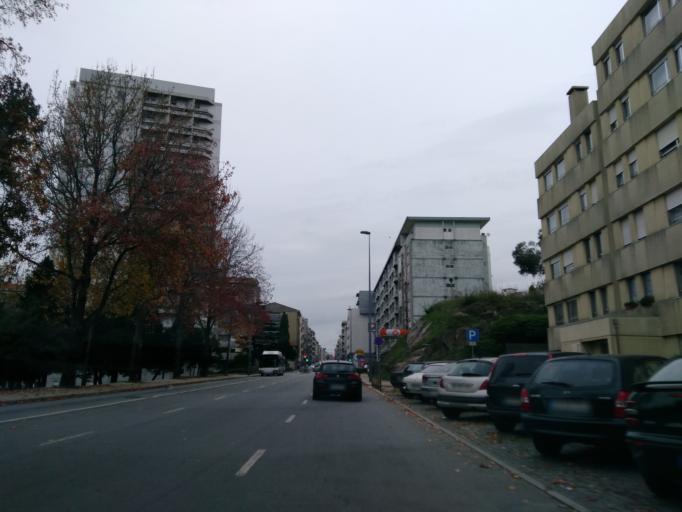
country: PT
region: Porto
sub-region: Porto
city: Porto
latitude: 41.1527
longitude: -8.5967
